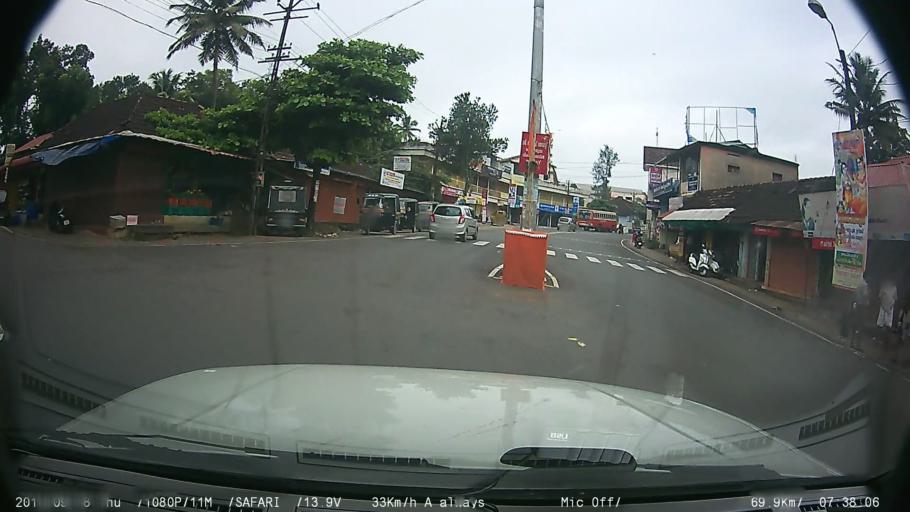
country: IN
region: Kerala
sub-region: Kottayam
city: Changanacheri
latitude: 9.4381
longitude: 76.5676
